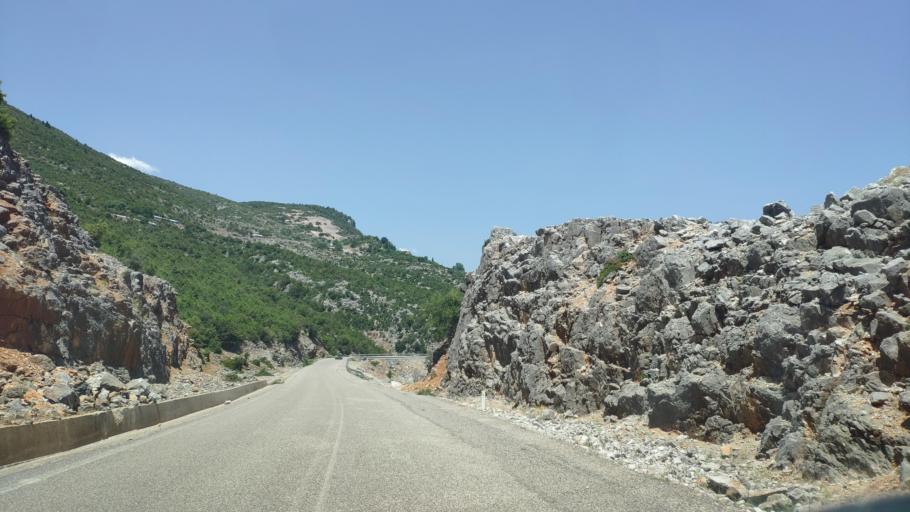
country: GR
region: Thessaly
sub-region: Nomos Kardhitsas
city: Anthiro
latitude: 39.1394
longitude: 21.3889
